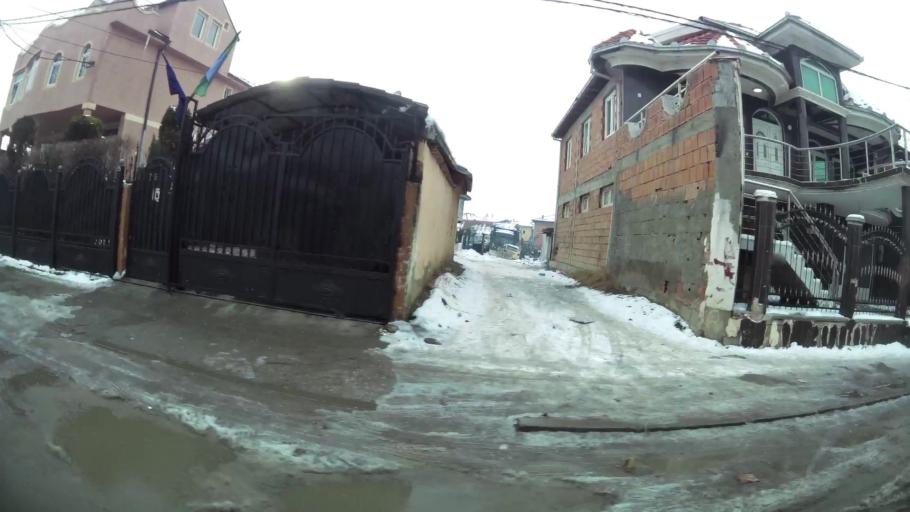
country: MK
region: Suto Orizari
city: Suto Orizare
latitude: 42.0434
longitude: 21.4206
